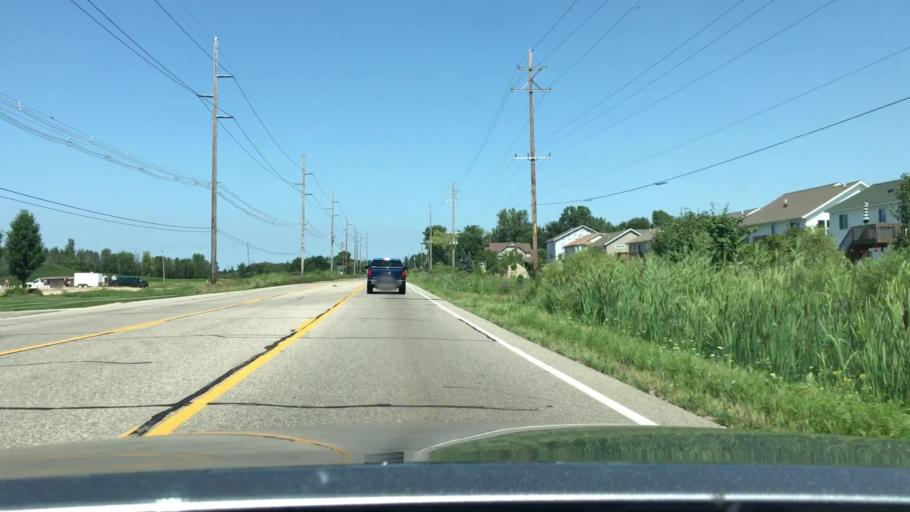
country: US
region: Michigan
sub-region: Ottawa County
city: Holland
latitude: 42.8354
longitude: -86.0787
